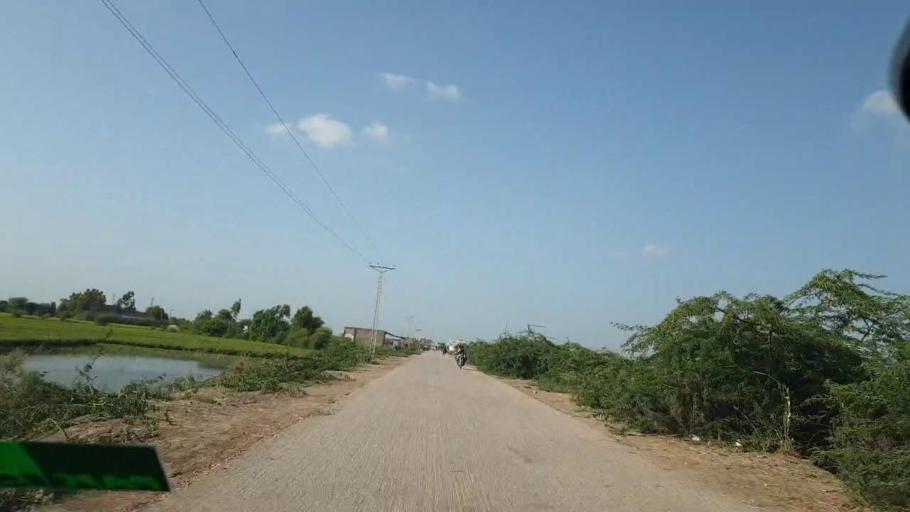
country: PK
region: Sindh
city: Naukot
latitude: 24.7505
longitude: 69.1974
